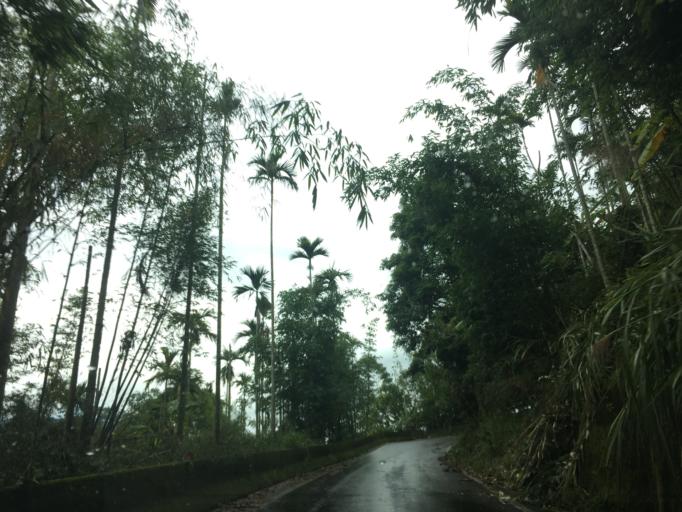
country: TW
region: Taiwan
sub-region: Yunlin
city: Douliu
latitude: 23.5616
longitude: 120.6534
